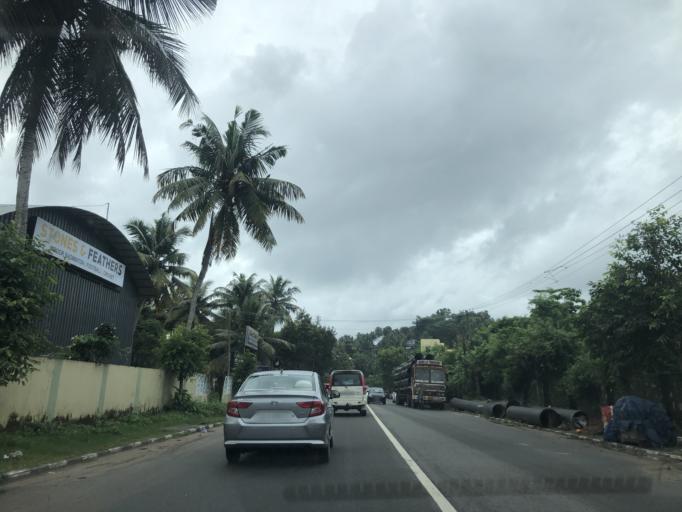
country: IN
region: Kerala
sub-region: Thiruvananthapuram
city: Thiruvananthapuram
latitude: 8.5139
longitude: 76.9149
